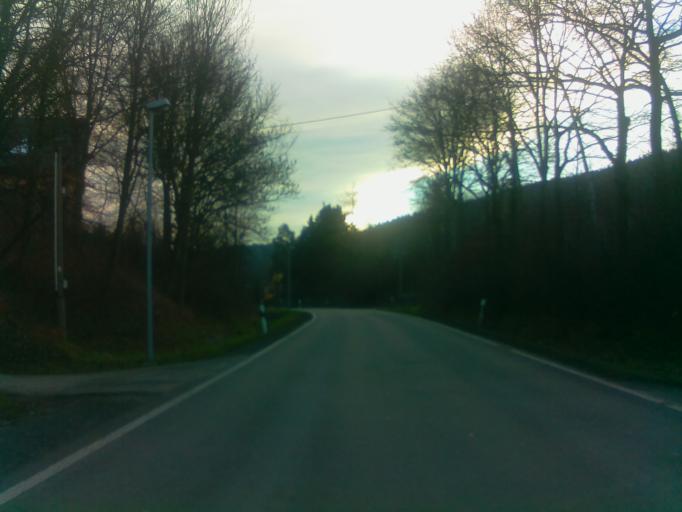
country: DE
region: Thuringia
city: Bad Blankenburg
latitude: 50.6738
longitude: 11.2813
